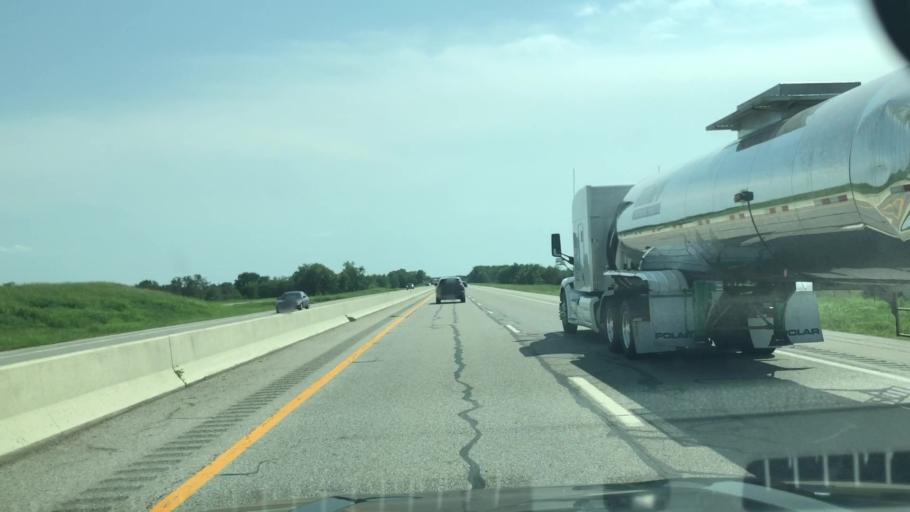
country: US
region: Oklahoma
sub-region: Ottawa County
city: Fairland
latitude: 36.7797
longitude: -94.8908
